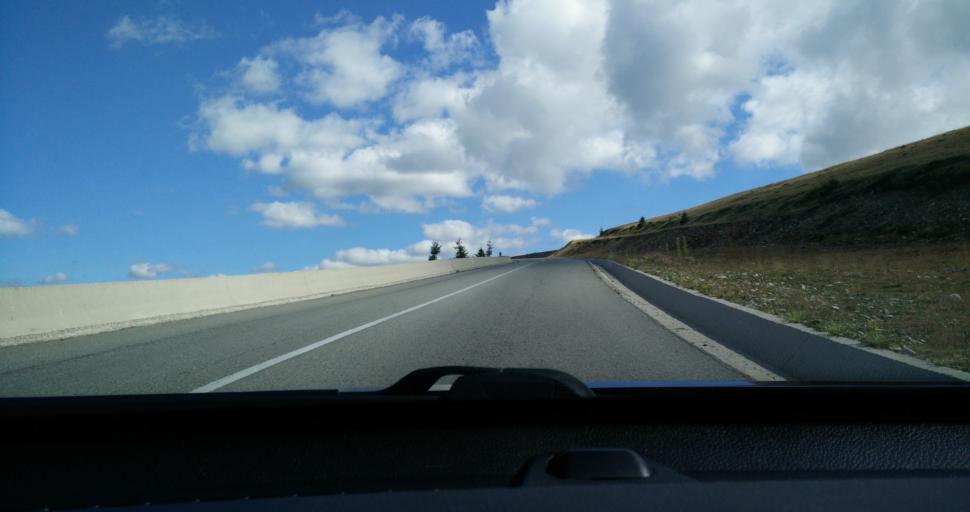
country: RO
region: Gorj
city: Novaci-Straini
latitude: 45.2497
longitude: 23.6939
